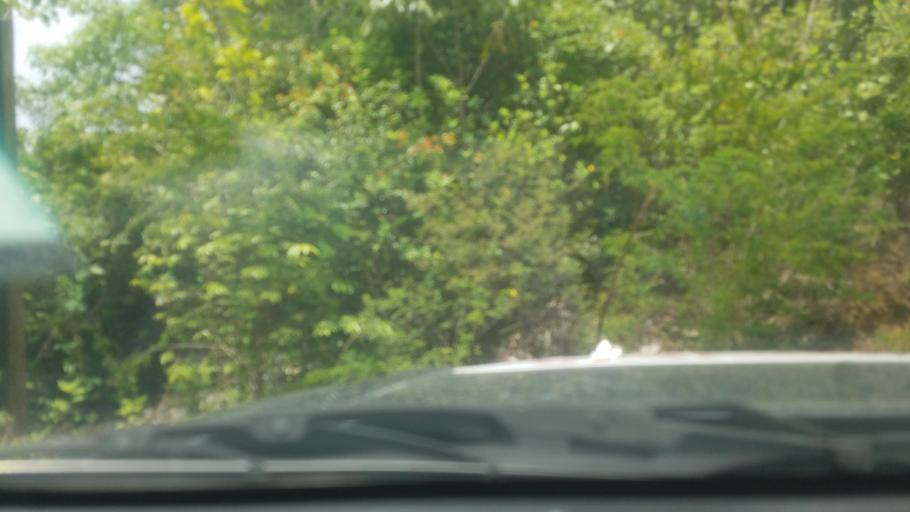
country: LC
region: Laborie Quarter
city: Laborie
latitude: 13.7608
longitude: -60.9941
